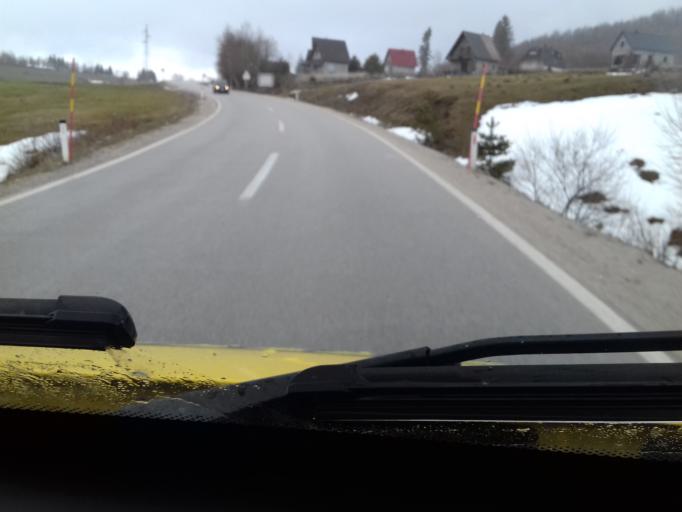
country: BA
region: Federation of Bosnia and Herzegovina
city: Novi Travnik
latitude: 44.1175
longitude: 17.5771
